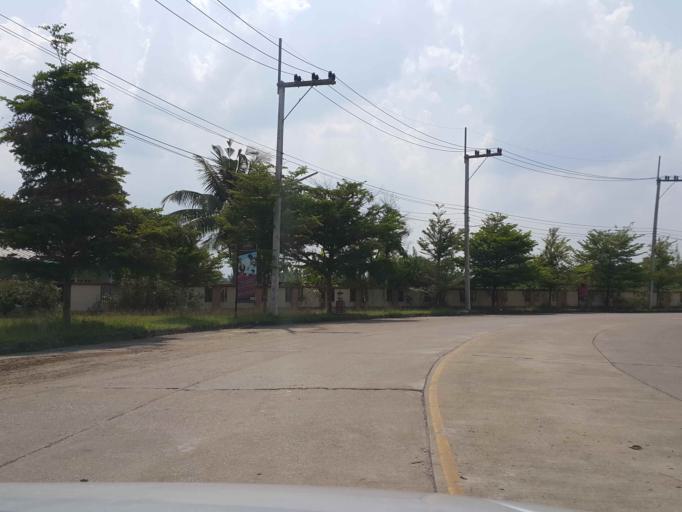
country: TH
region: Chiang Mai
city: Hang Dong
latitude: 18.7018
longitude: 98.9410
